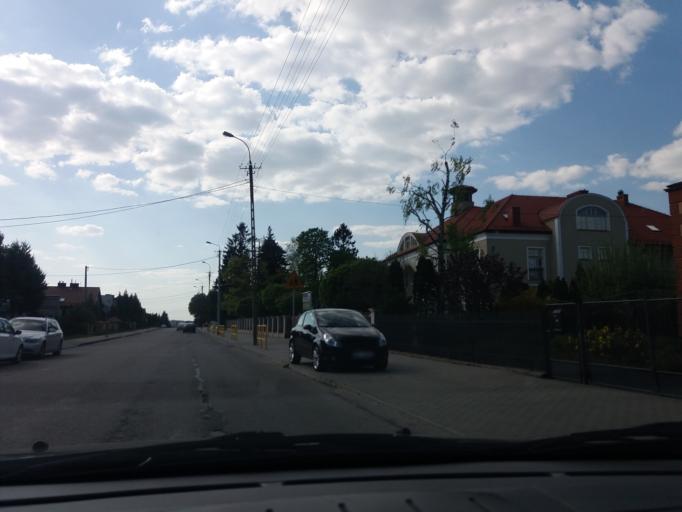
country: PL
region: Masovian Voivodeship
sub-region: Powiat mlawski
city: Mlawa
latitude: 53.1148
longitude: 20.3688
